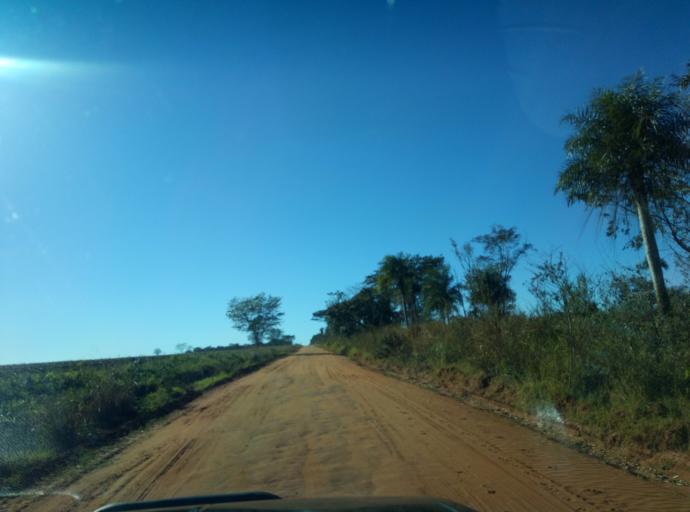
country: PY
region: Caaguazu
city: Doctor Cecilio Baez
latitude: -25.1610
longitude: -56.2768
